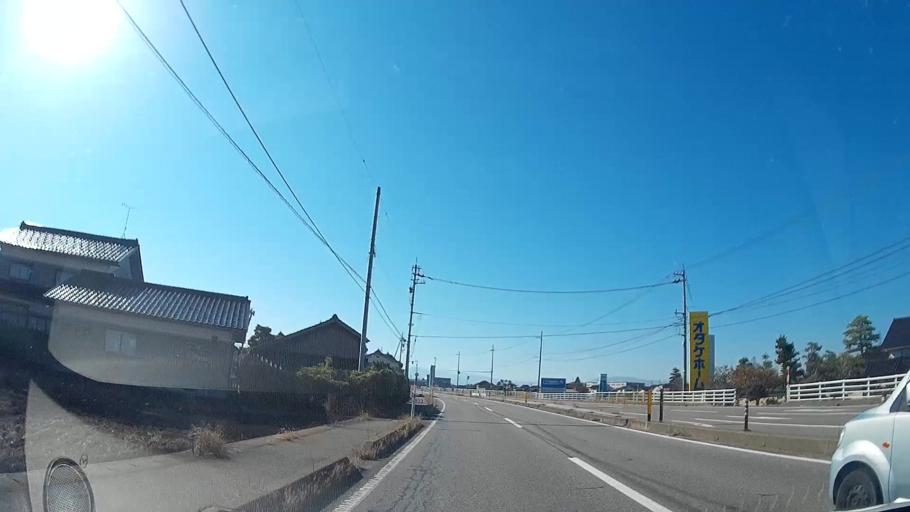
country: JP
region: Toyama
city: Takaoka
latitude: 36.6666
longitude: 136.9732
